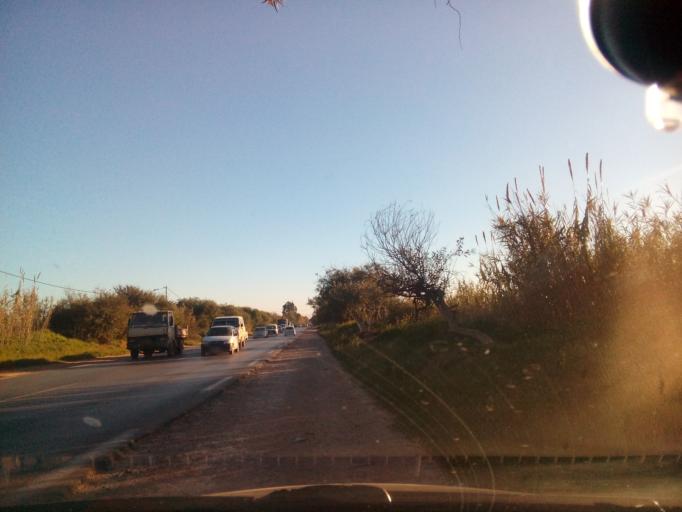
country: DZ
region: Mostaganem
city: Mostaganem
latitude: 35.8236
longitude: 0.1693
